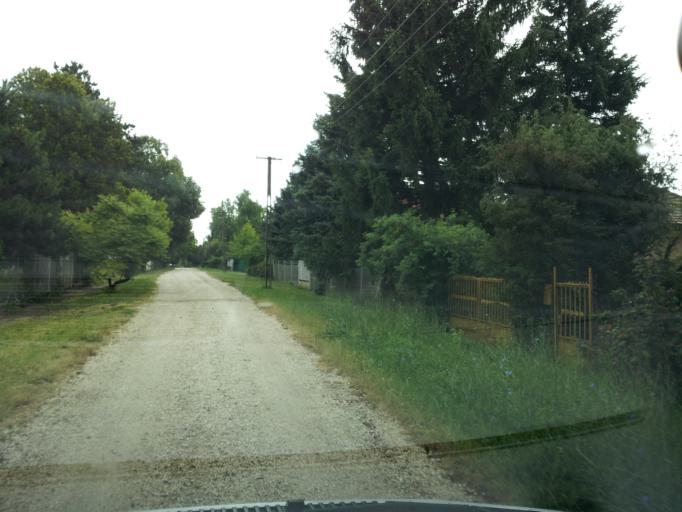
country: HU
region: Veszprem
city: Balatonkenese
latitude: 47.0220
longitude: 18.1514
